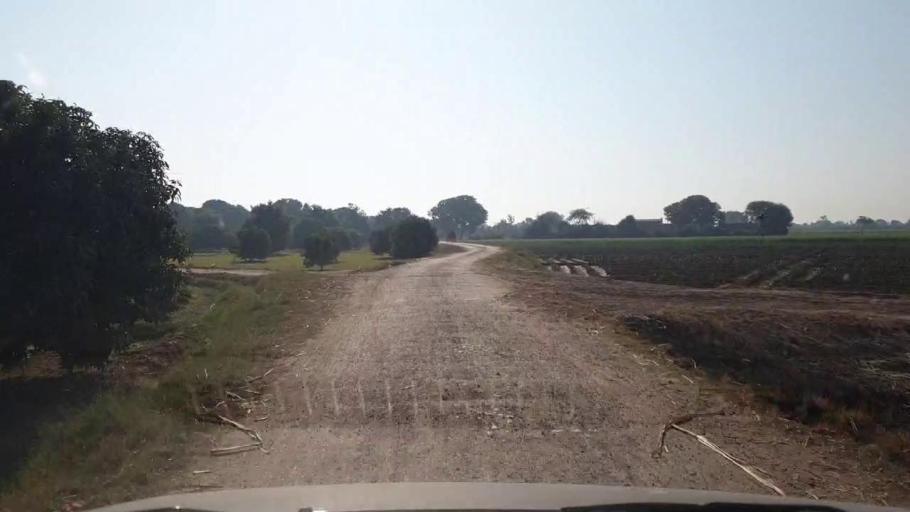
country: PK
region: Sindh
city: Tando Jam
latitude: 25.4313
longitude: 68.6040
